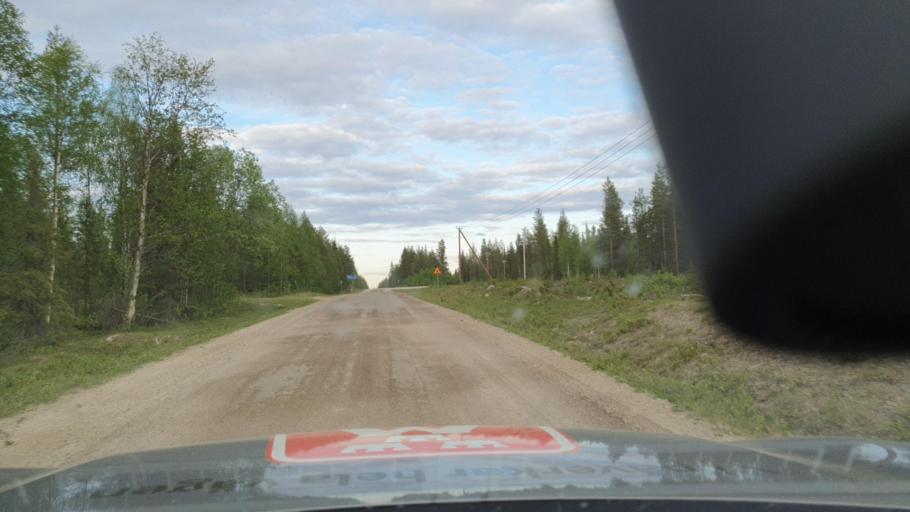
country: SE
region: Norrbotten
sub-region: Gallivare Kommun
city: Gaellivare
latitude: 66.7409
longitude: 21.1330
